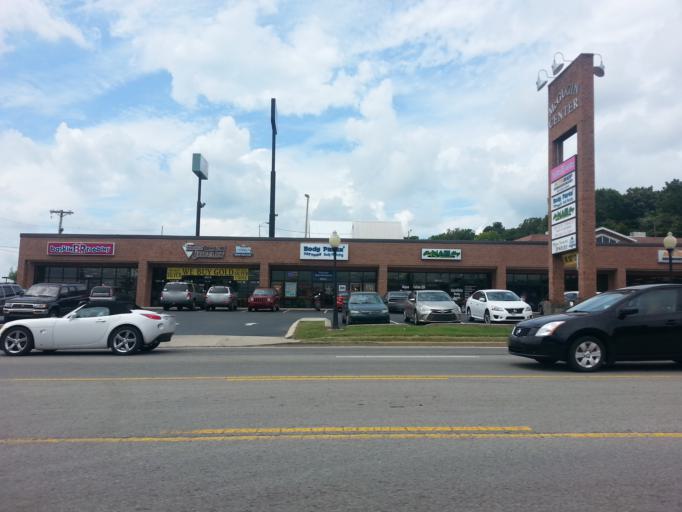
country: US
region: Tennessee
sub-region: Putnam County
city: Cookeville
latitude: 36.1399
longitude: -85.5014
